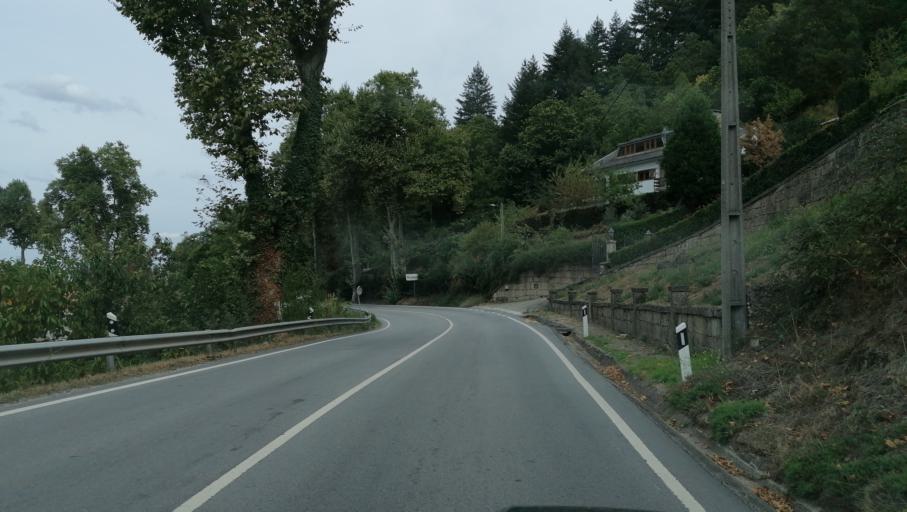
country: PT
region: Vila Real
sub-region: Vila Pouca de Aguiar
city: Vila Pouca de Aguiar
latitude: 41.5122
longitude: -7.6255
